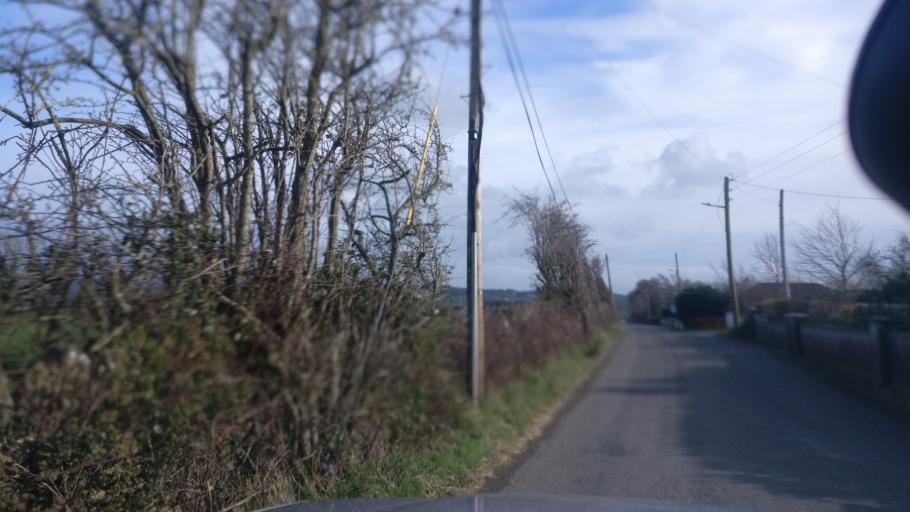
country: IE
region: Leinster
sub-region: Kilkenny
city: Thomastown
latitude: 52.5262
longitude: -7.1631
